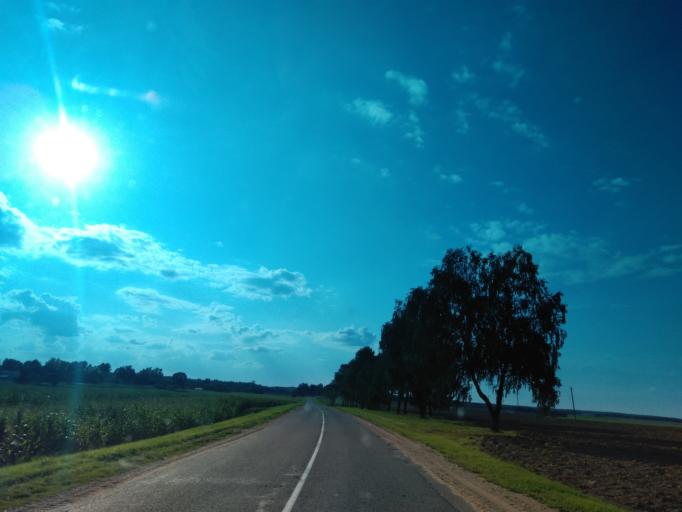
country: BY
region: Minsk
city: Kapyl'
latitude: 53.2038
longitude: 27.0391
